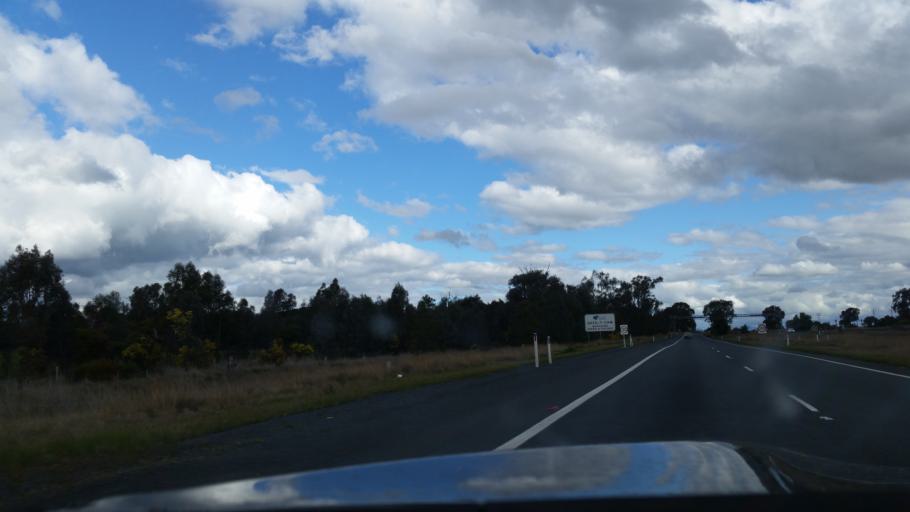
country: AU
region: New South Wales
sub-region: Albury Municipality
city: Lavington
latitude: -35.9646
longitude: 147.0050
